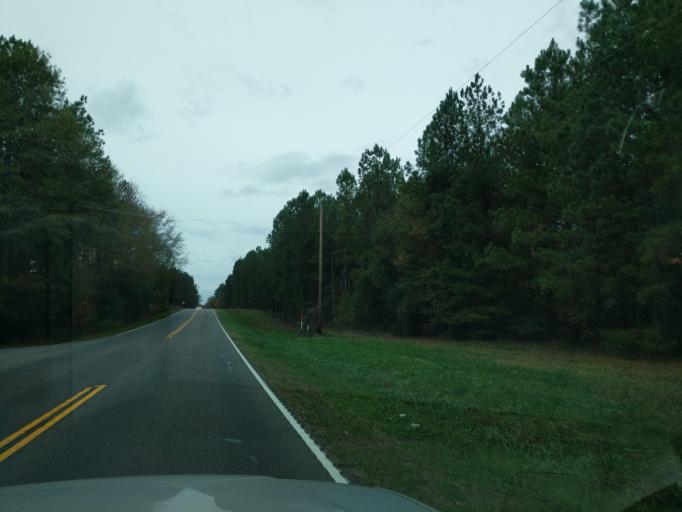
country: US
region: South Carolina
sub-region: Lexington County
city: Batesburg
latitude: 33.9337
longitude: -81.6026
